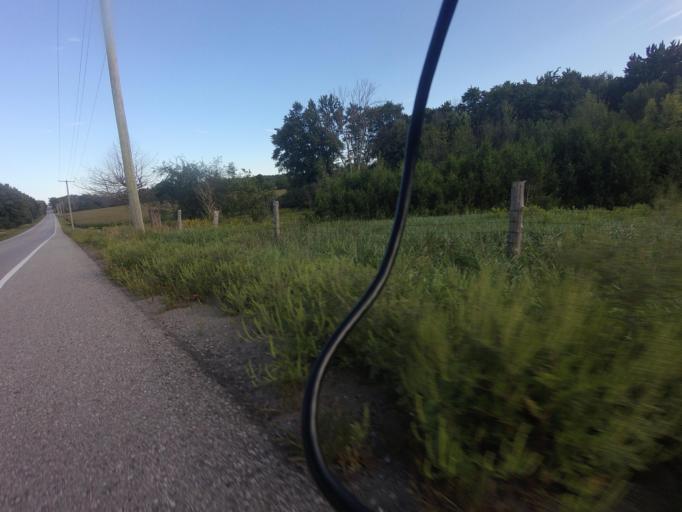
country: CA
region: Ontario
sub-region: Wellington County
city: Guelph
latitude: 43.5812
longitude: -80.3373
